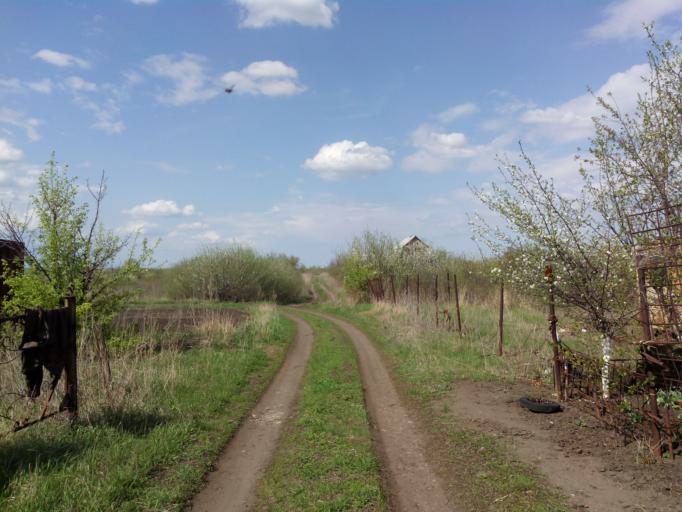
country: RU
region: Voronezj
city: Borisoglebsk
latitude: 51.3758
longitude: 42.1487
